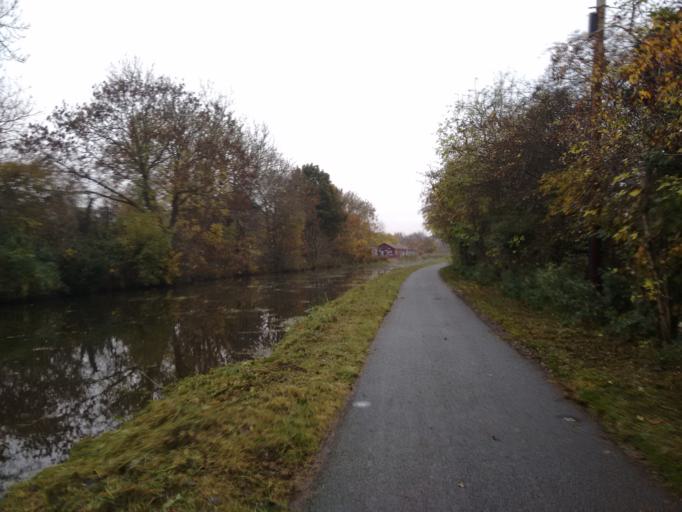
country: GB
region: Scotland
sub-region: Edinburgh
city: Colinton
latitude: 55.9300
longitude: -3.2280
